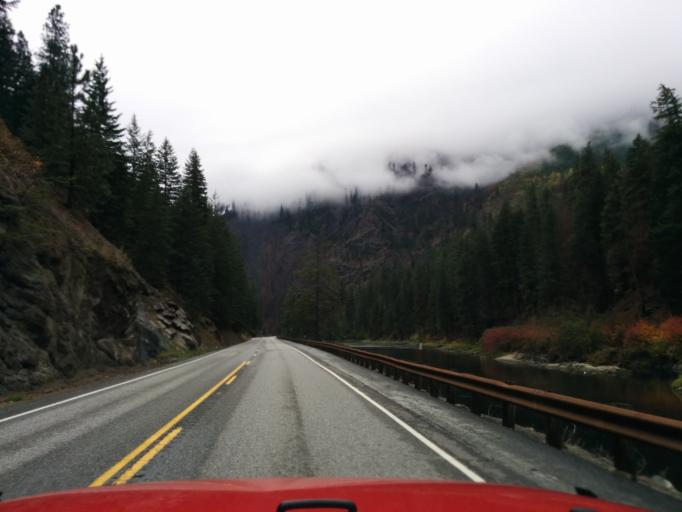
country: US
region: Washington
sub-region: Chelan County
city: Leavenworth
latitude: 47.6715
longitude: -120.7353
